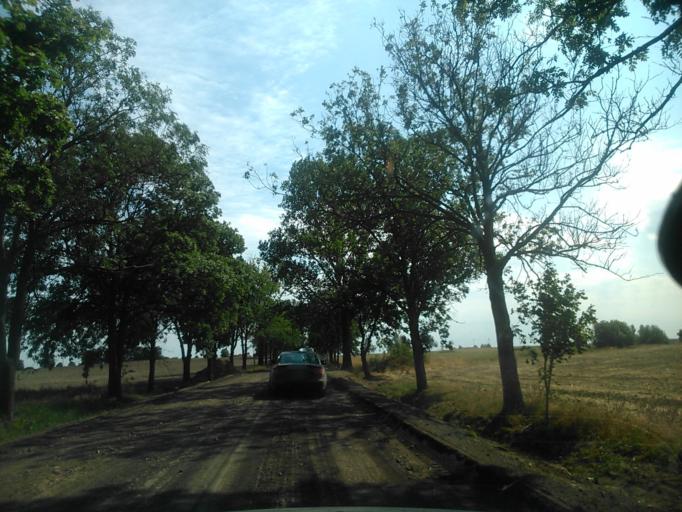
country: PL
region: Warmian-Masurian Voivodeship
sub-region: Powiat dzialdowski
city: Dzialdowo
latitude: 53.2088
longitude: 20.2322
